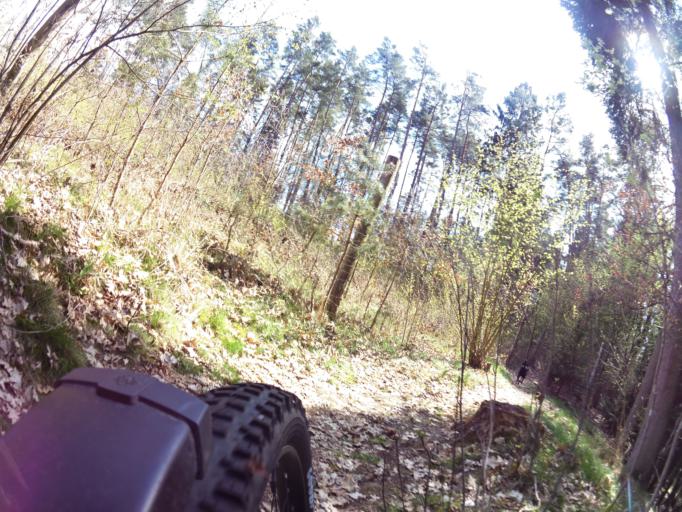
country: PL
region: West Pomeranian Voivodeship
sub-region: Powiat lobeski
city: Resko
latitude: 53.8060
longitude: 15.4551
